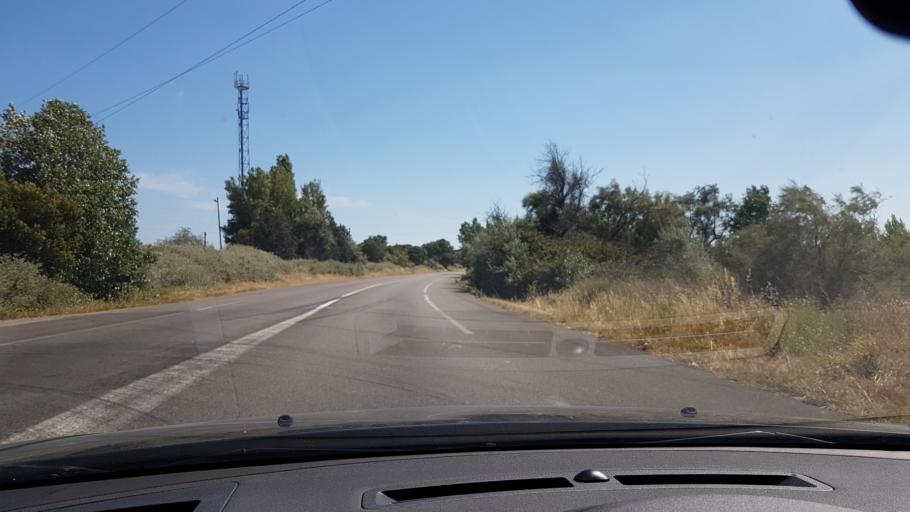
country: FR
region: Provence-Alpes-Cote d'Azur
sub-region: Departement des Bouches-du-Rhone
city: Port-Saint-Louis-du-Rhone
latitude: 43.4462
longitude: 4.8382
